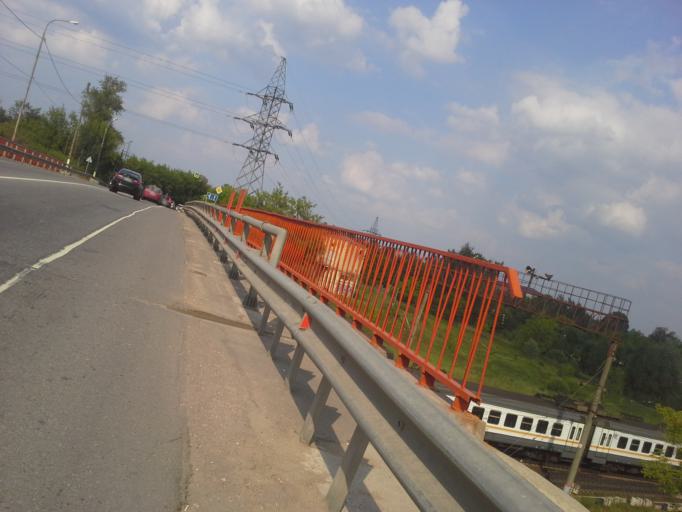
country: RU
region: Moskovskaya
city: Istra
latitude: 55.9133
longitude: 36.8170
